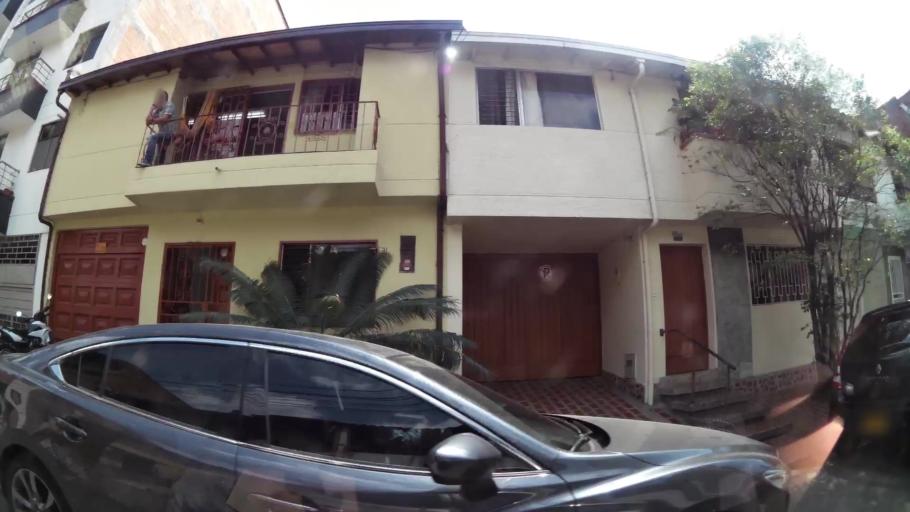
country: CO
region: Antioquia
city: Envigado
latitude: 6.1754
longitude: -75.5876
